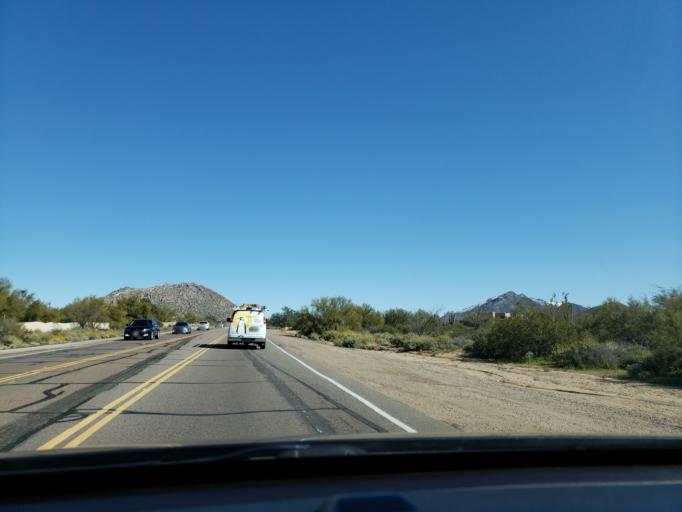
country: US
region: Arizona
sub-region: Maricopa County
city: Carefree
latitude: 33.7126
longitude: -111.8801
